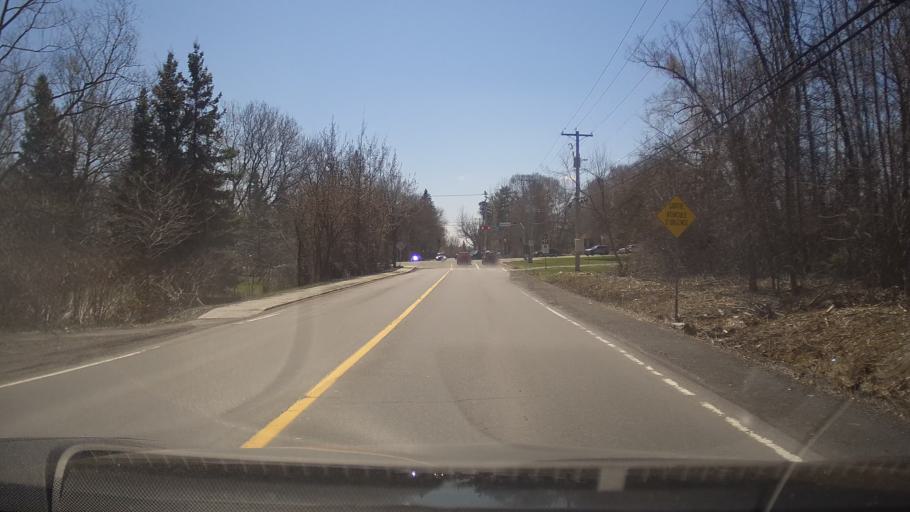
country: CA
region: Ontario
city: Bells Corners
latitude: 45.4069
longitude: -75.8074
